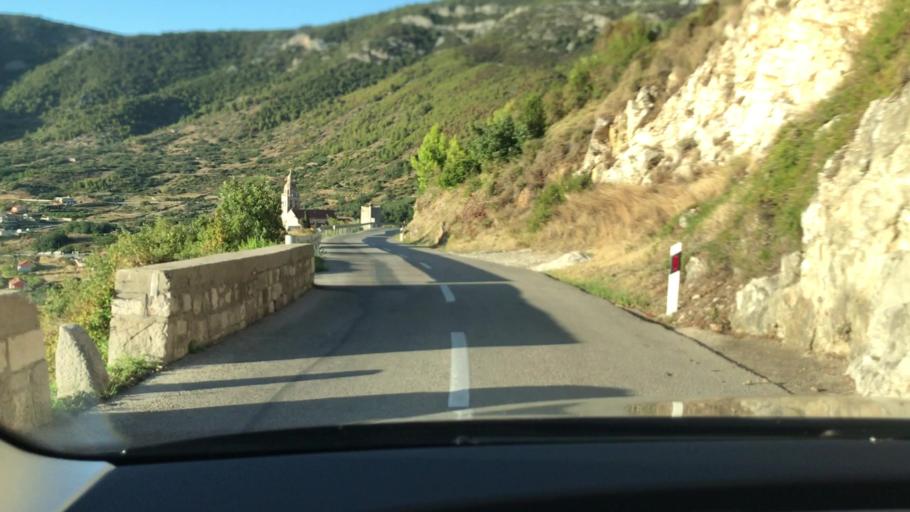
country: HR
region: Splitsko-Dalmatinska
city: Komiza
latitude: 43.0376
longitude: 16.0955
